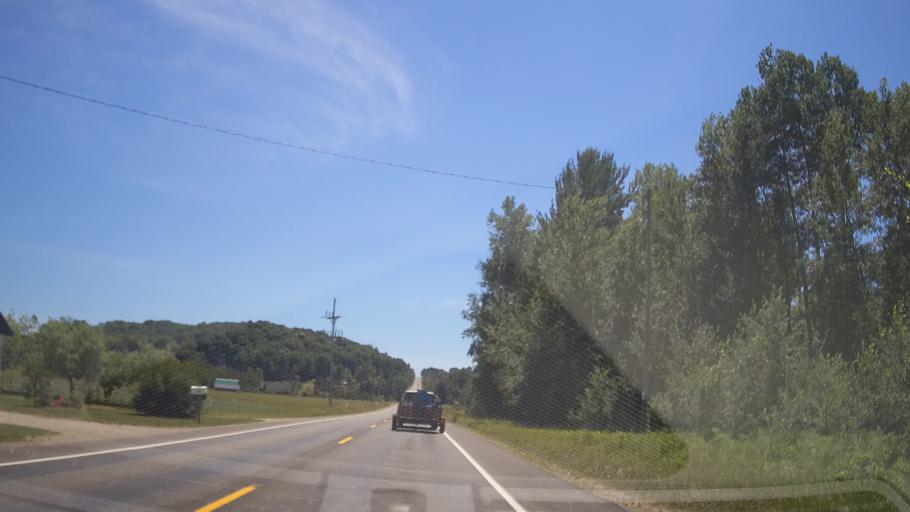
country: US
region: Michigan
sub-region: Grand Traverse County
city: Traverse City
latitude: 44.6317
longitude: -85.6964
